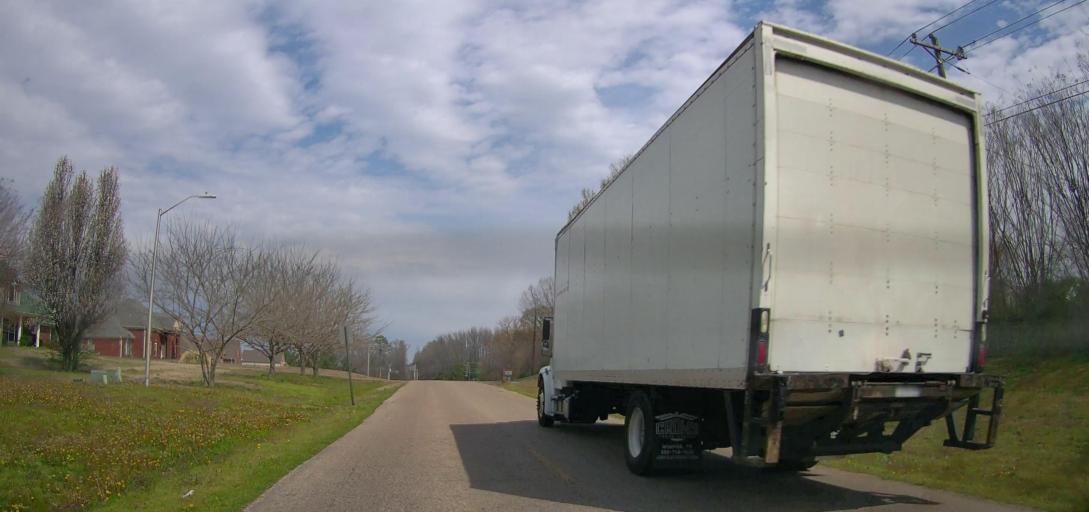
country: US
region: Mississippi
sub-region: De Soto County
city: Olive Branch
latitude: 34.9920
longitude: -89.8484
